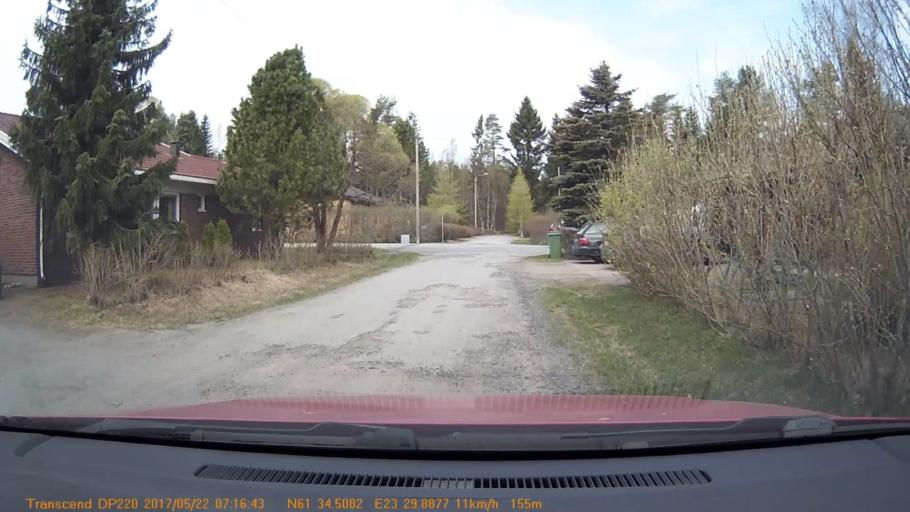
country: FI
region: Pirkanmaa
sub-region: Tampere
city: Yloejaervi
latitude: 61.5754
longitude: 23.4973
